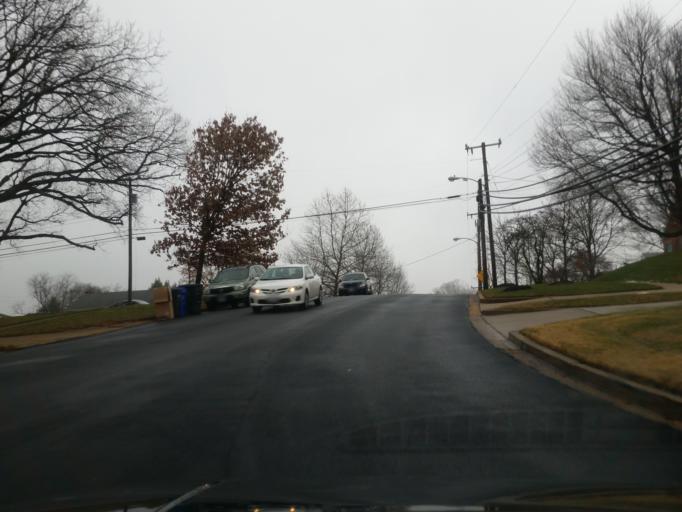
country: US
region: Virginia
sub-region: Fairfax County
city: Seven Corners
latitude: 38.9084
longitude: -77.1429
